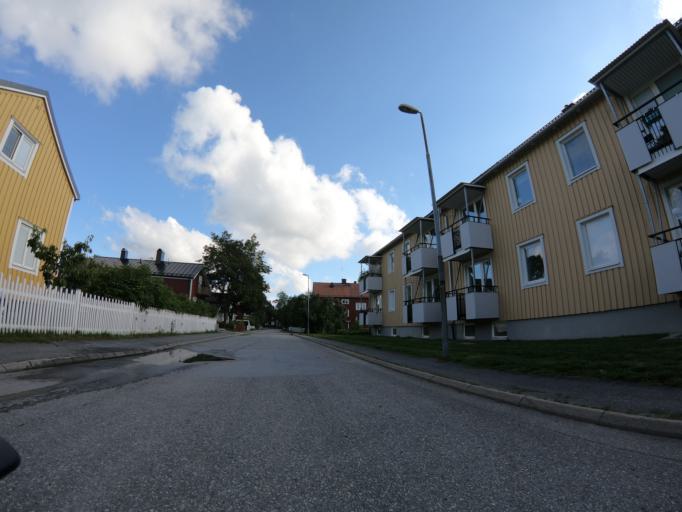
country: SE
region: Vaesterbotten
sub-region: Umea Kommun
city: Umea
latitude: 63.8292
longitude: 20.2793
